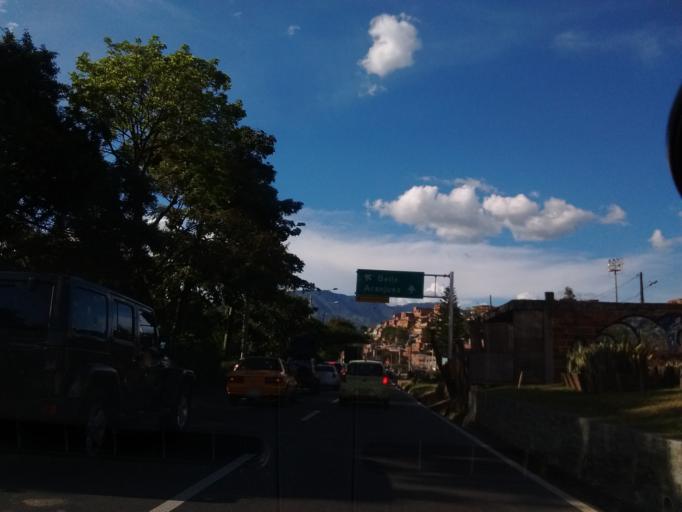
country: CO
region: Antioquia
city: Medellin
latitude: 6.2795
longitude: -75.5683
